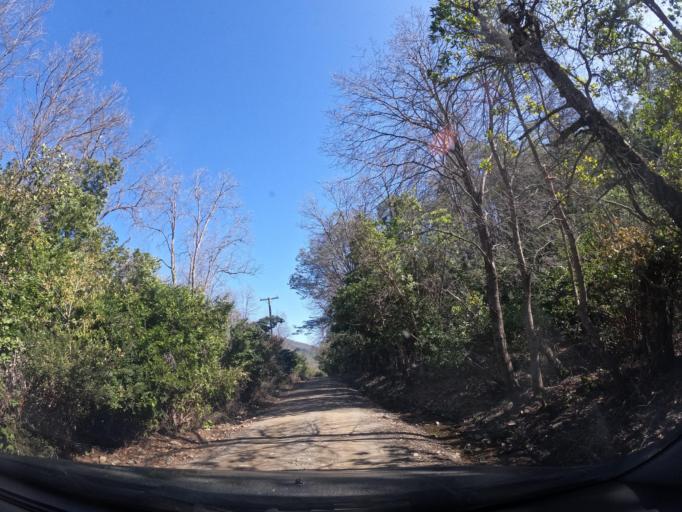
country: CL
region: Maule
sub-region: Provincia de Linares
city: Longavi
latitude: -36.2472
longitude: -71.3371
